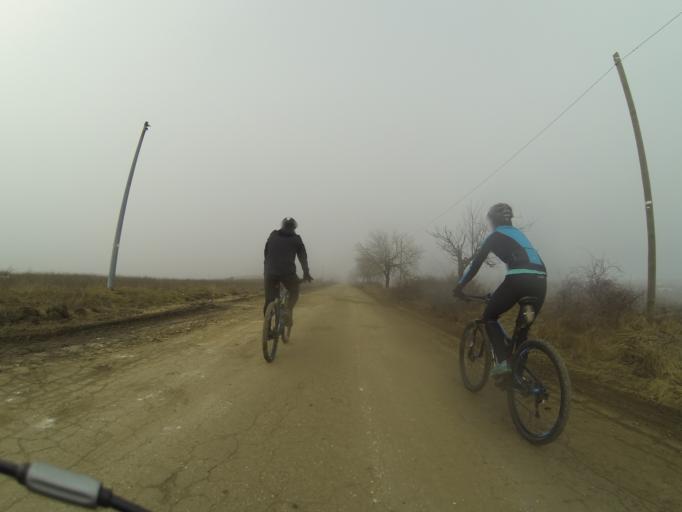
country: RO
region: Mehedinti
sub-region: Comuna Baclesu
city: Baclesu
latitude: 44.4844
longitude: 23.1024
